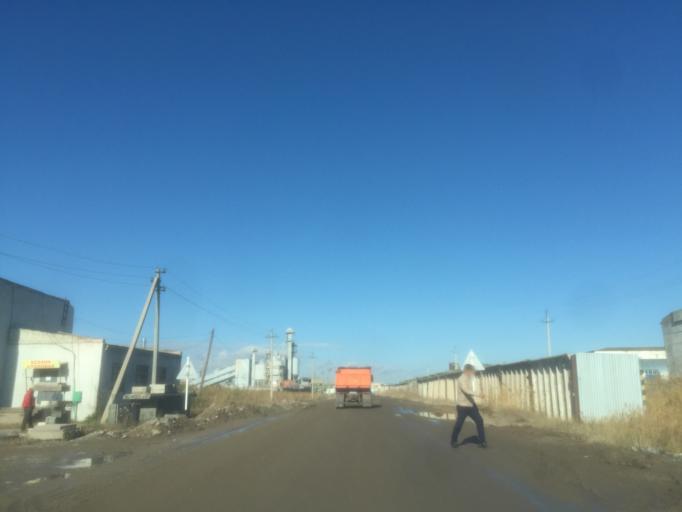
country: KZ
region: Astana Qalasy
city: Astana
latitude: 51.2122
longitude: 71.3525
